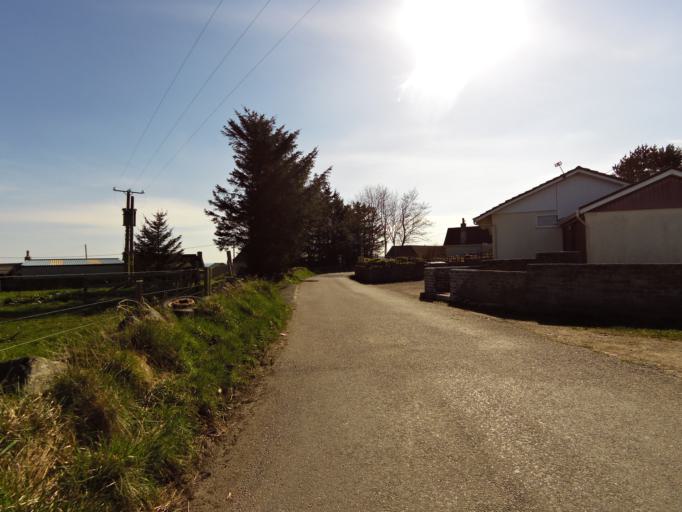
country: GB
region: Scotland
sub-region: Aberdeenshire
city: Portlethen
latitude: 57.0693
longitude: -2.1051
